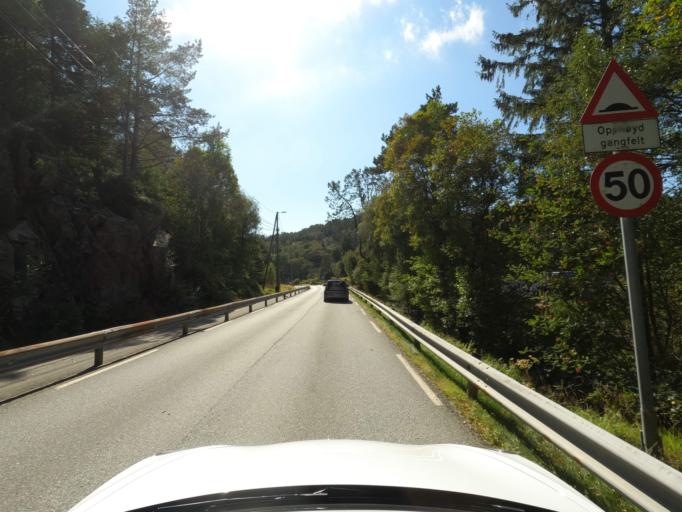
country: NO
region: Hordaland
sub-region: Bergen
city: Sandsli
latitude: 60.2379
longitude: 5.3017
